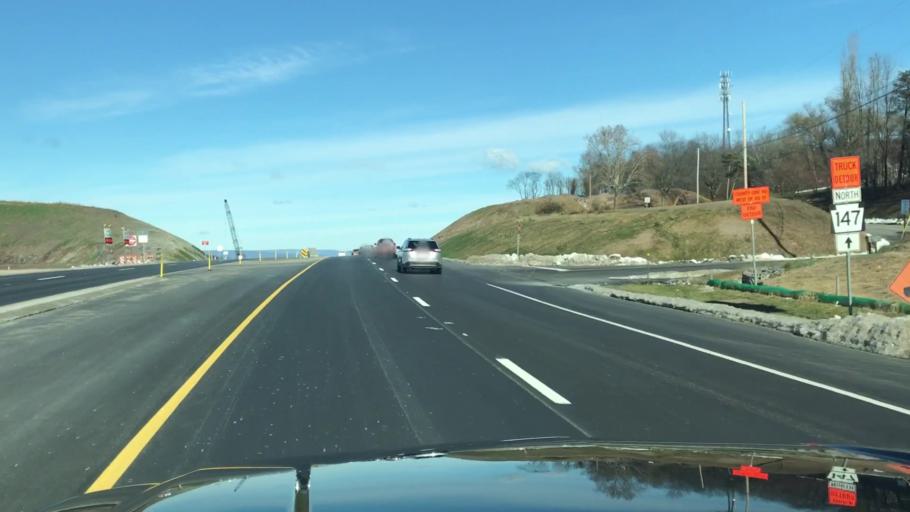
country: US
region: Pennsylvania
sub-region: Snyder County
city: Shamokin Dam
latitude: 40.8853
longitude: -76.8419
